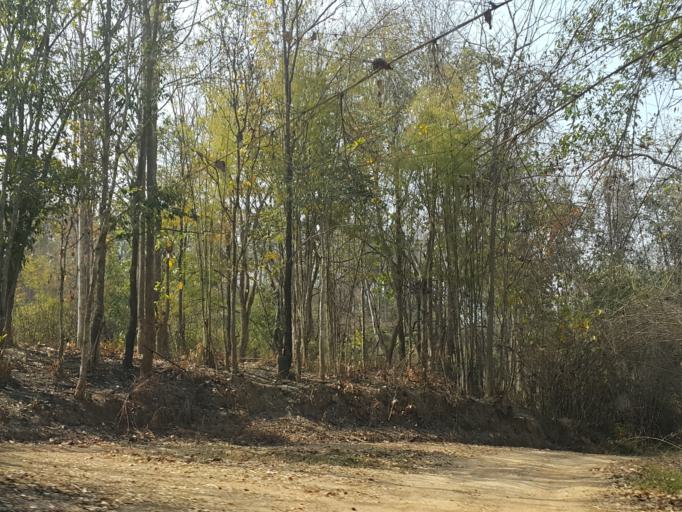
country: TH
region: Chiang Mai
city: Hang Dong
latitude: 18.7176
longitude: 98.8559
